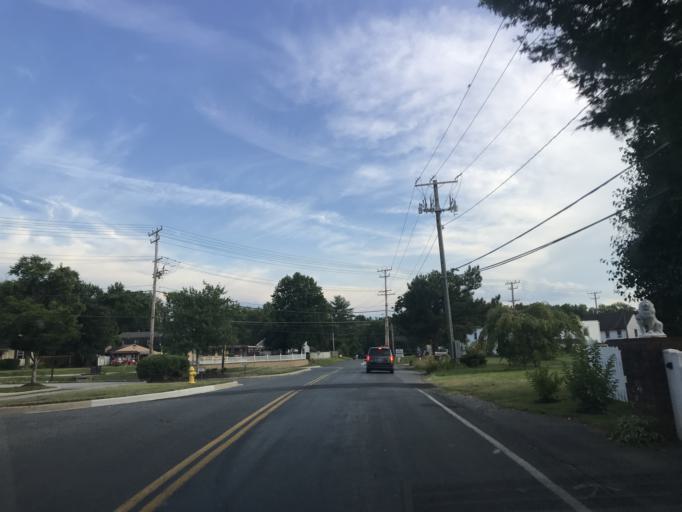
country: US
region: Maryland
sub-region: Harford County
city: Perryman
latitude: 39.4904
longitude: -76.2114
